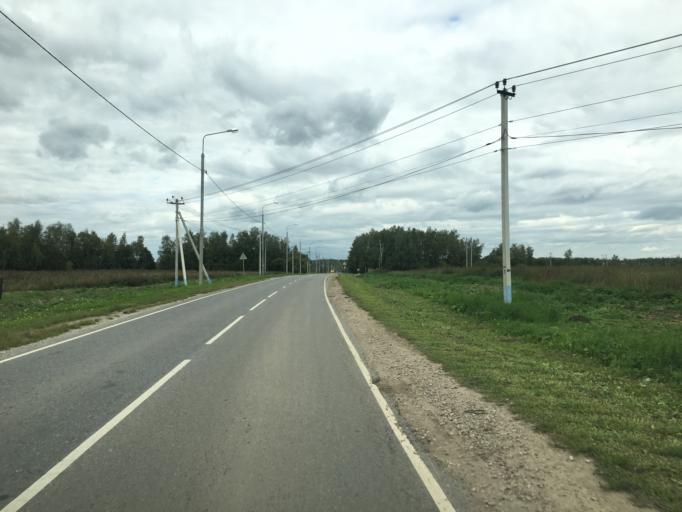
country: RU
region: Moskovskaya
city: Vatutinki
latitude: 55.4827
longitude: 37.4003
